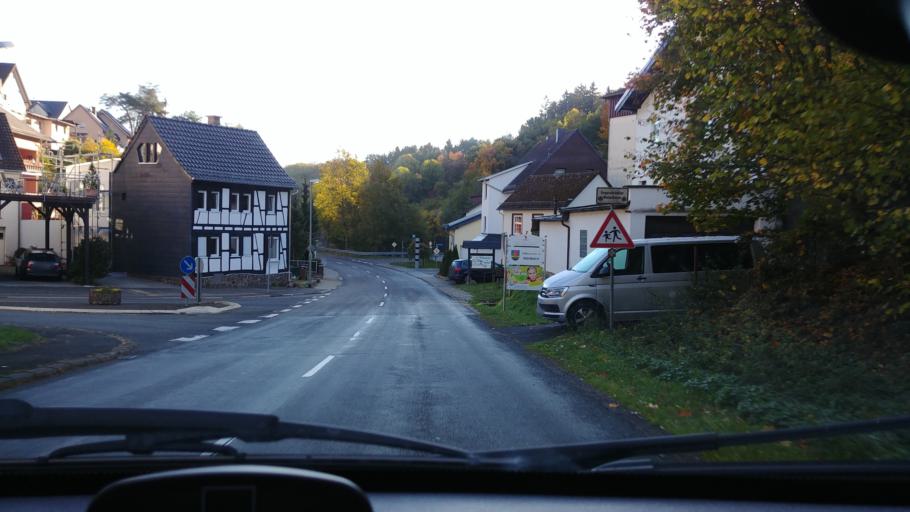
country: DE
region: Hesse
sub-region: Regierungsbezirk Darmstadt
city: Bad Schwalbach
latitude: 50.1542
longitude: 8.0448
